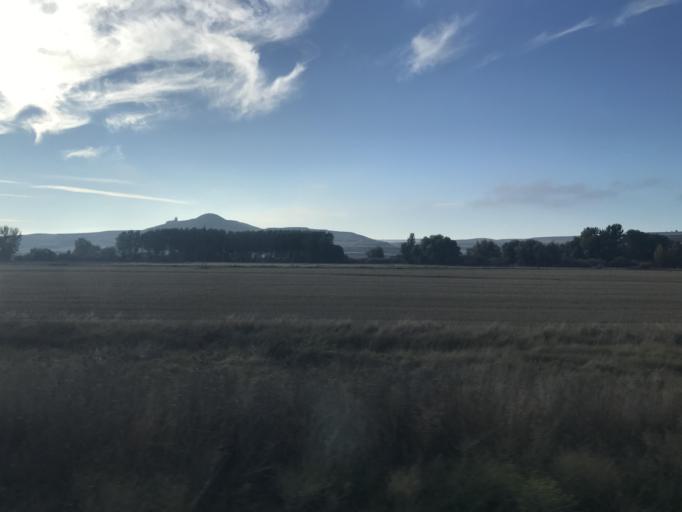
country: ES
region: Castille and Leon
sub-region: Provincia de Burgos
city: Estepar
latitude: 42.2649
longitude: -3.9128
